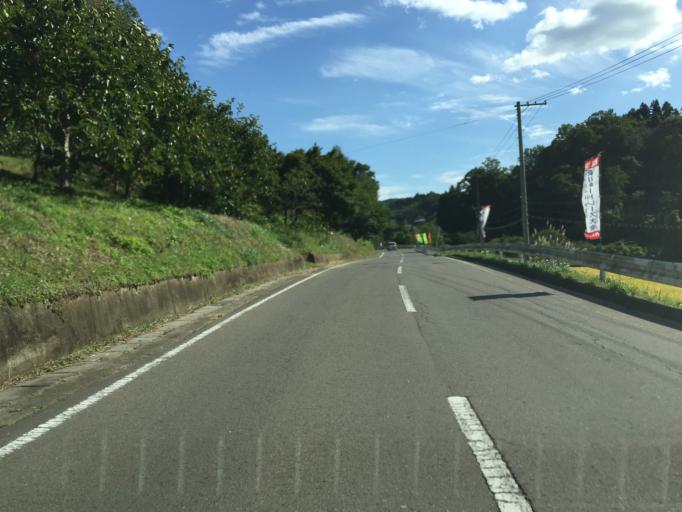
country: JP
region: Fukushima
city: Yanagawamachi-saiwaicho
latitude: 37.8483
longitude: 140.6530
